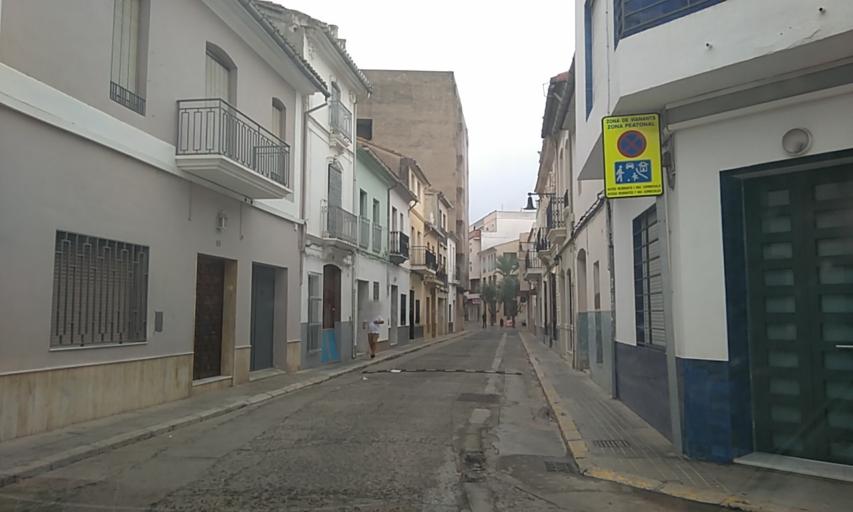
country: ES
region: Valencia
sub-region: Provincia de Valencia
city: L'Alcudia
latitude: 39.1970
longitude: -0.5079
